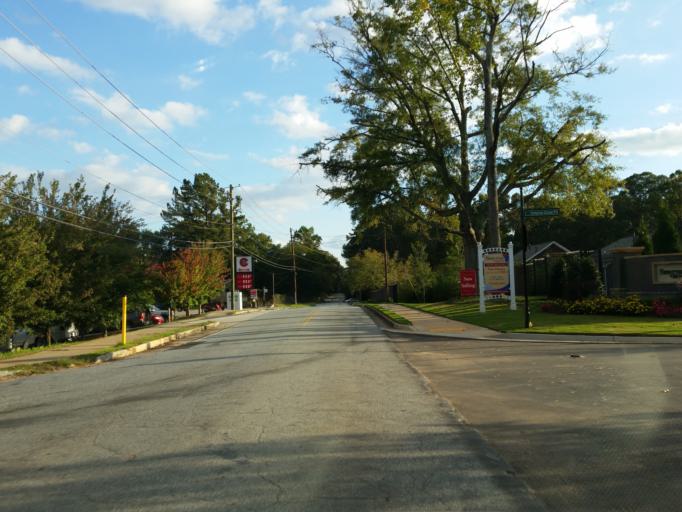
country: US
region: Georgia
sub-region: Cobb County
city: Fair Oaks
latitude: 33.8911
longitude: -84.5402
